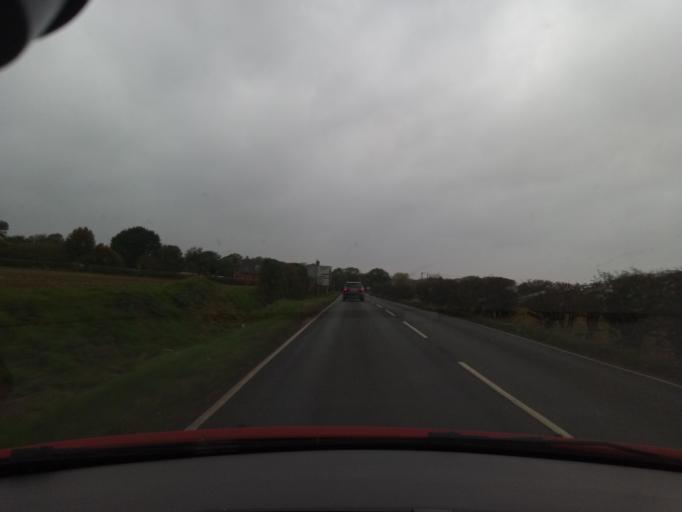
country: GB
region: England
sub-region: Suffolk
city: Kedington
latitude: 52.0556
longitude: 0.4954
